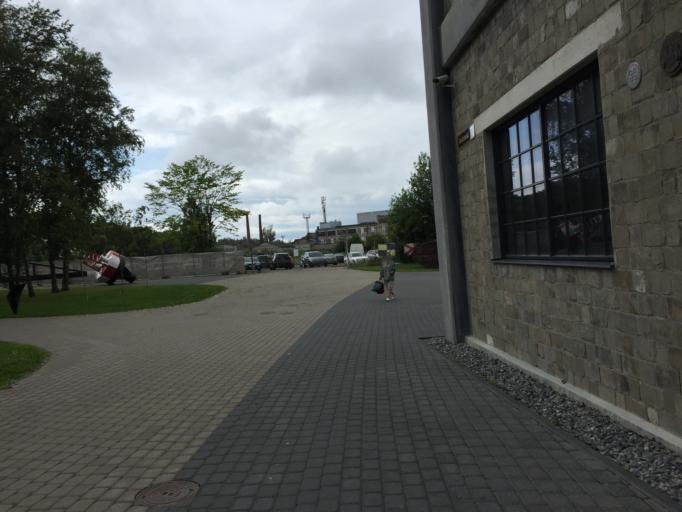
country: EE
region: Harju
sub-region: Tallinna linn
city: Tallinn
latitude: 59.4509
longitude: 24.7380
